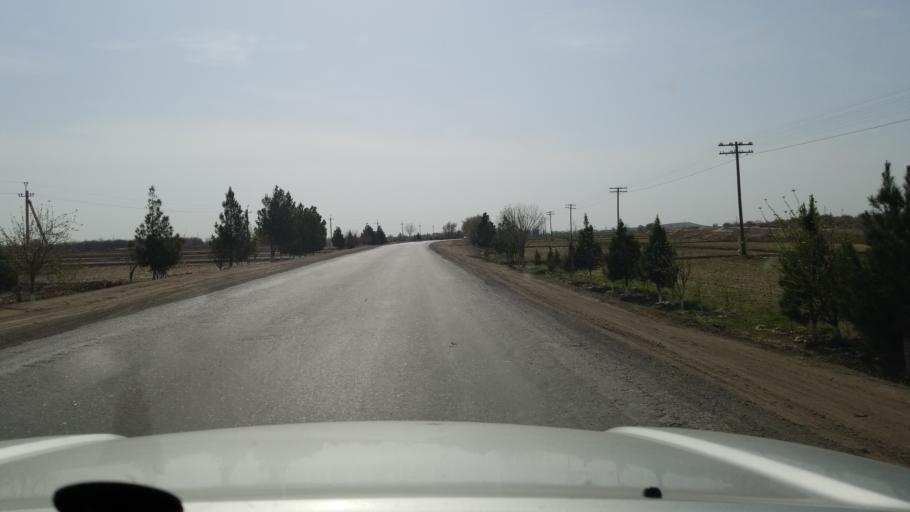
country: TM
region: Lebap
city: Sayat
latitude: 38.8501
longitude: 63.8093
